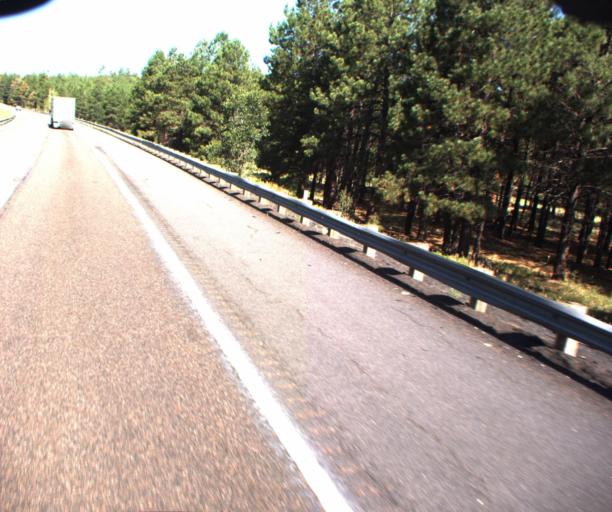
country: US
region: Arizona
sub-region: Coconino County
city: Parks
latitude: 35.2521
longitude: -111.9001
